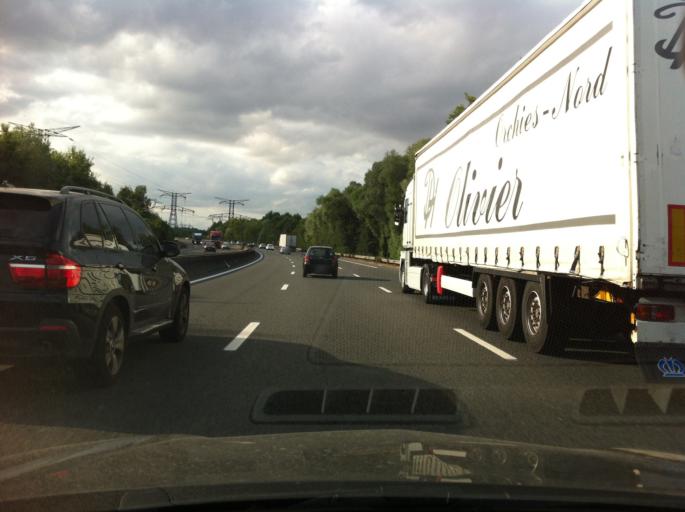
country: FR
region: Ile-de-France
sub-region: Departement de Seine-et-Marne
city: Pomponne
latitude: 48.8897
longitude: 2.6677
